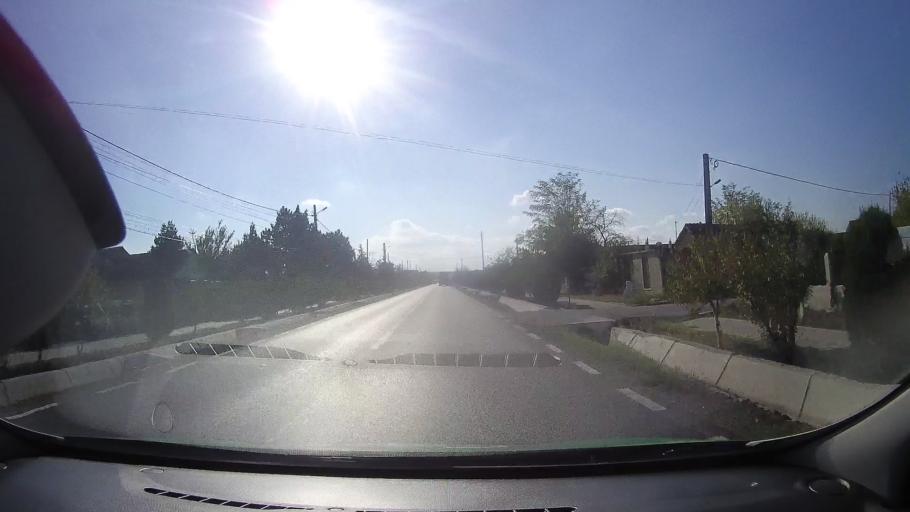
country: RO
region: Tulcea
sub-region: Comuna Baia
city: Baia
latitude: 44.7301
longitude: 28.6814
